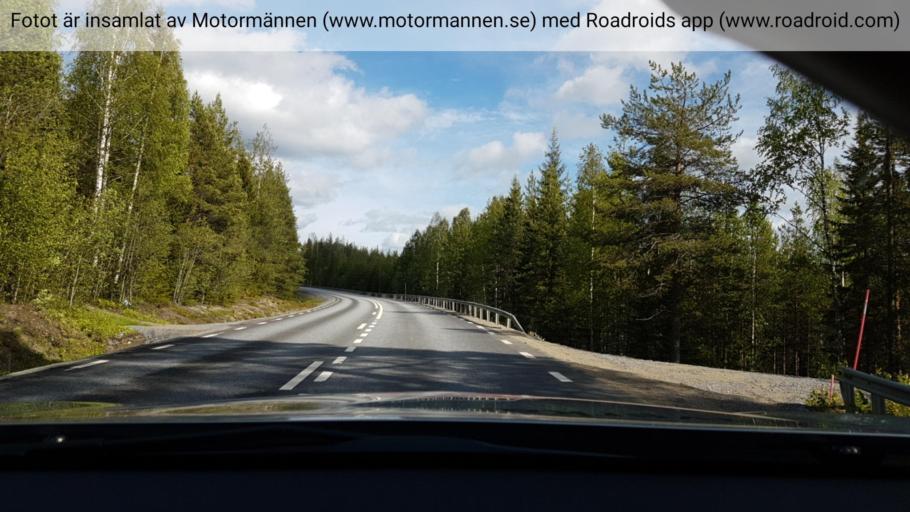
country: SE
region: Vaesterbotten
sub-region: Bjurholms Kommun
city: Bjurholm
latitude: 63.9156
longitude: 19.1582
